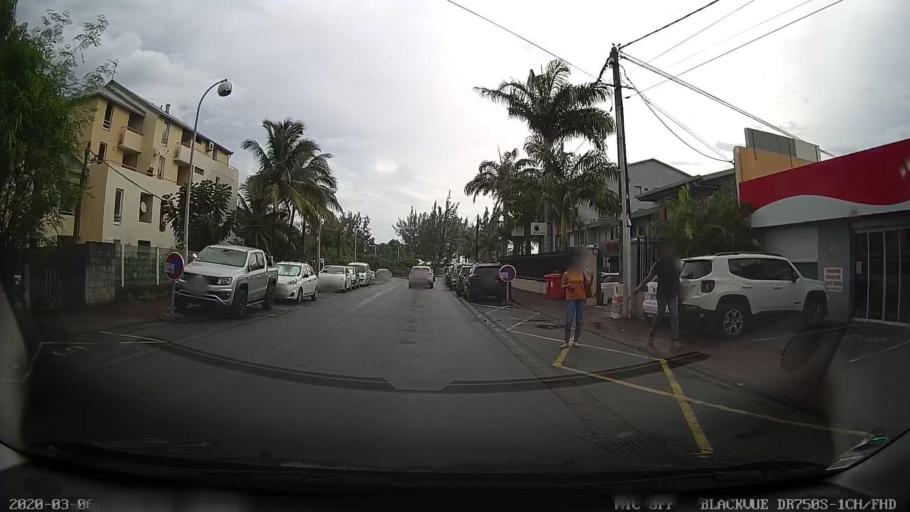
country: RE
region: Reunion
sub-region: Reunion
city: Saint-Pierre
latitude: -21.3377
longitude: 55.4589
